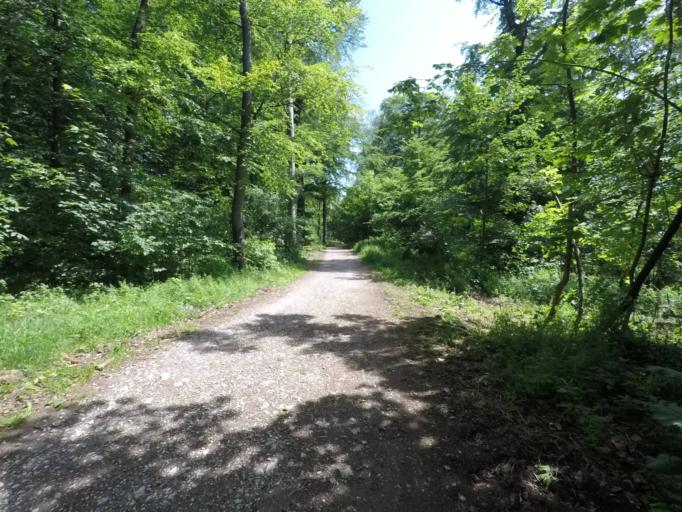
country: DE
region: North Rhine-Westphalia
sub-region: Regierungsbezirk Detmold
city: Bielefeld
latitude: 52.0144
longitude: 8.4854
